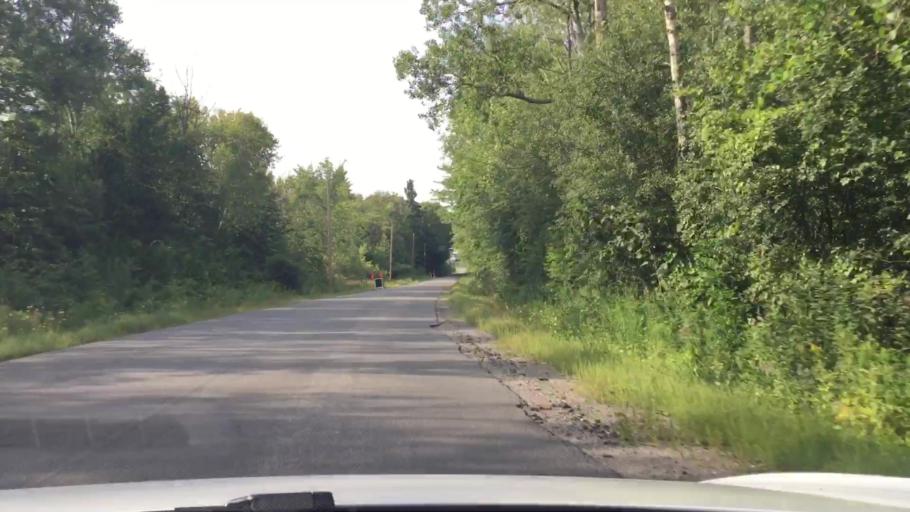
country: CA
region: Ontario
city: Oshawa
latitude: 43.9435
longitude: -78.7492
